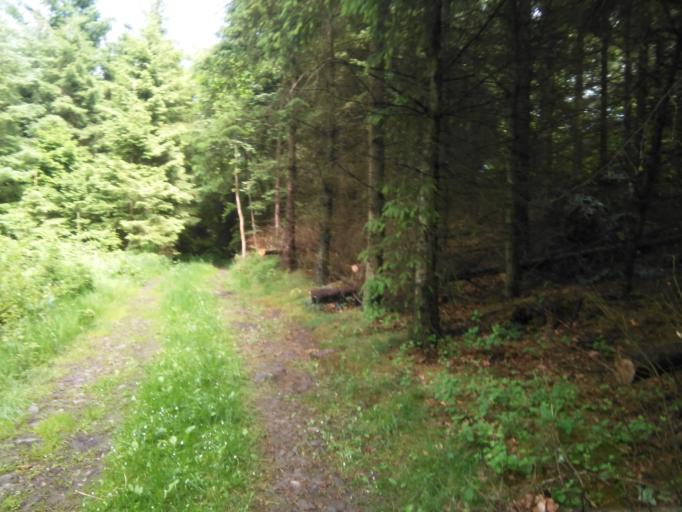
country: DK
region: Capital Region
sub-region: Bornholm Kommune
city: Nexo
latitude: 55.0963
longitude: 15.1035
